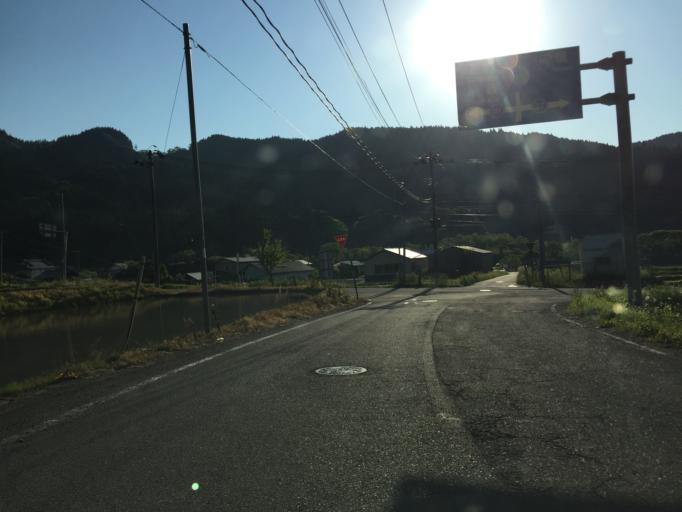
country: JP
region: Ibaraki
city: Daigo
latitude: 36.9301
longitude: 140.4459
